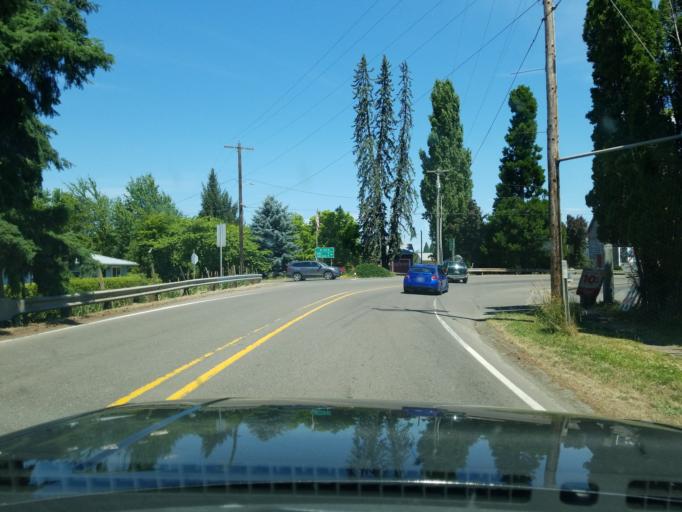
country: US
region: Oregon
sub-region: Yamhill County
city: Yamhill
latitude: 45.3453
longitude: -123.1877
